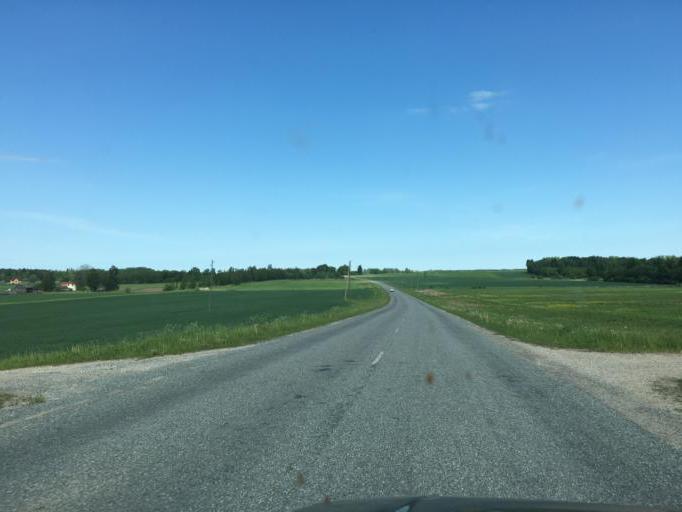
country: LV
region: Talsu Rajons
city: Valdemarpils
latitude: 57.3655
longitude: 22.4884
